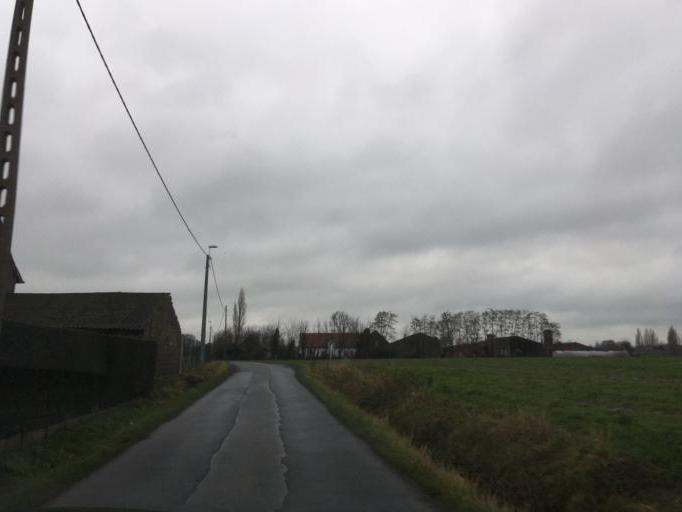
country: BE
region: Flanders
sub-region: Provincie West-Vlaanderen
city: Hooglede
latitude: 50.9706
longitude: 3.1079
